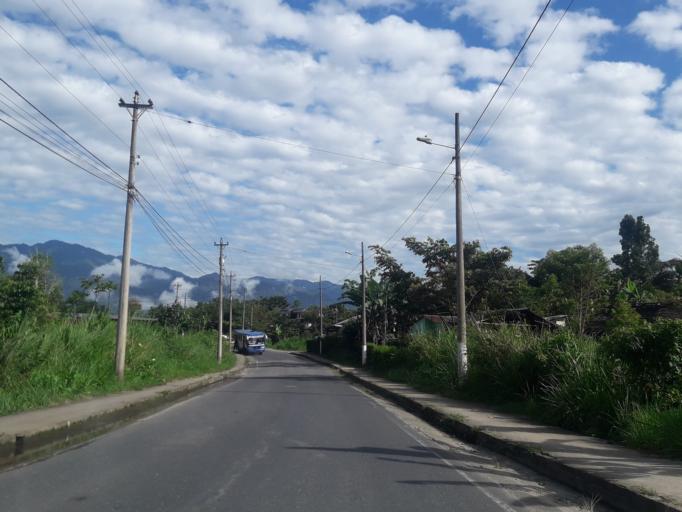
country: EC
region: Napo
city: Tena
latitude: -0.9857
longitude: -77.8363
